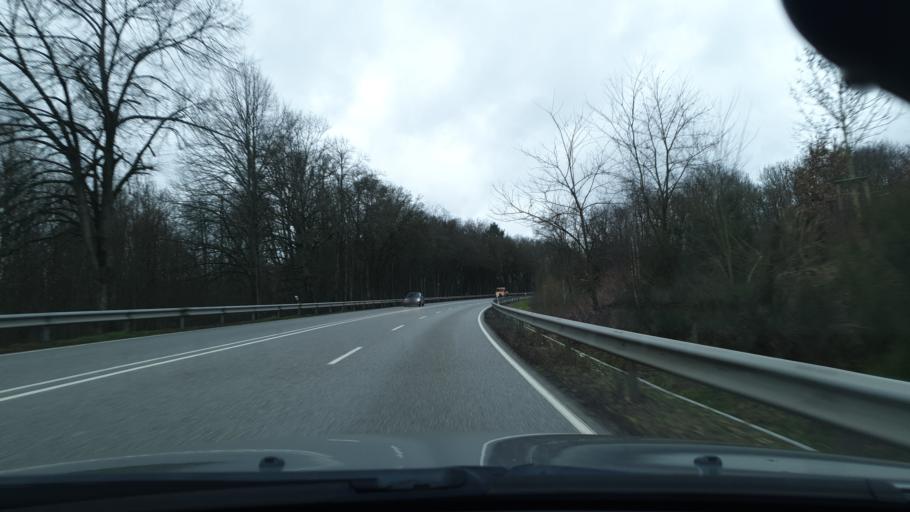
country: DE
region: Rheinland-Pfalz
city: Zweibrucken
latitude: 49.2608
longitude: 7.3760
